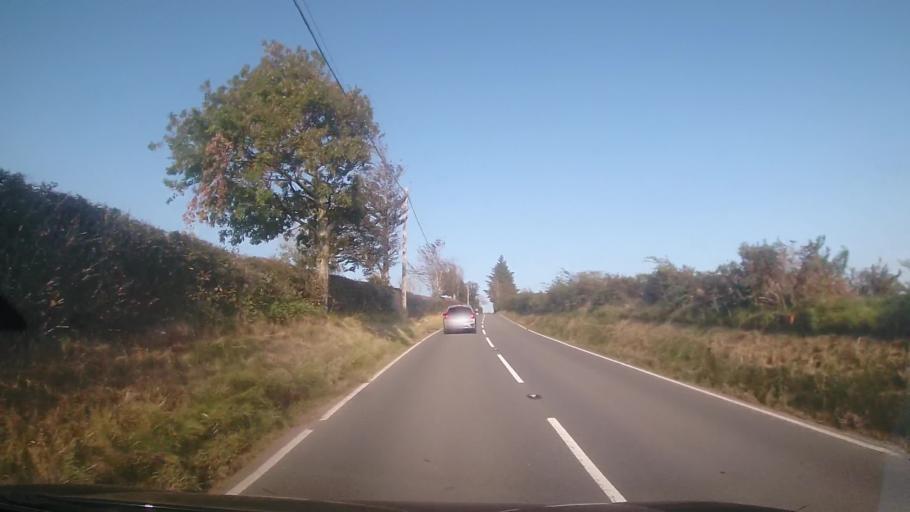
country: GB
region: Wales
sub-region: County of Ceredigion
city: Lledrod
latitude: 52.2935
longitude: -3.8579
